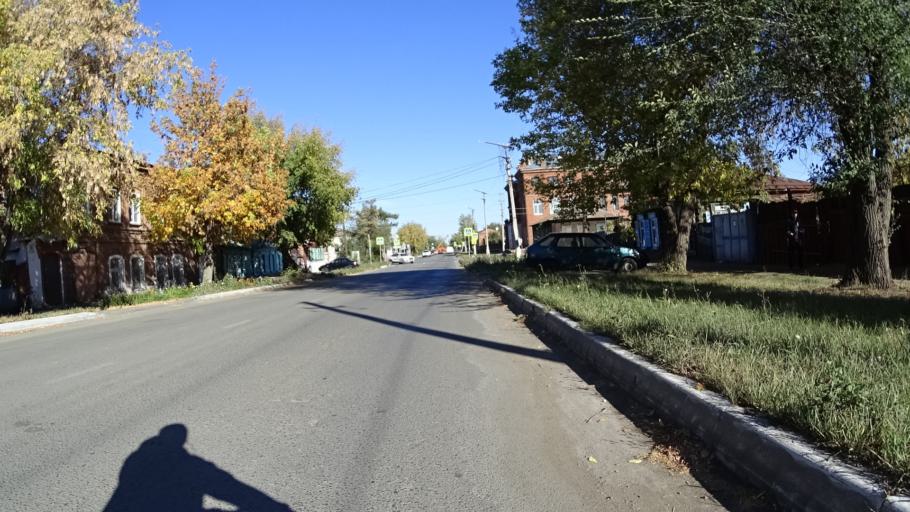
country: RU
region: Chelyabinsk
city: Troitsk
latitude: 54.0820
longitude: 61.5467
